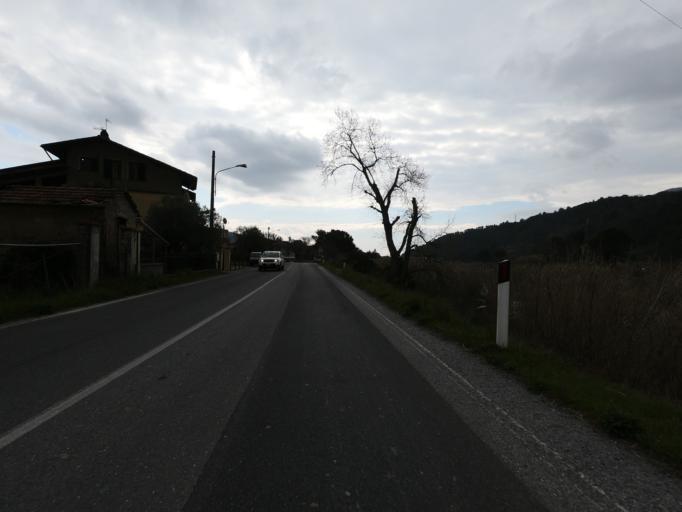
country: IT
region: Liguria
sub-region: Provincia di Imperia
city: Villa Faraldi
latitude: 43.9924
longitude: 8.1206
